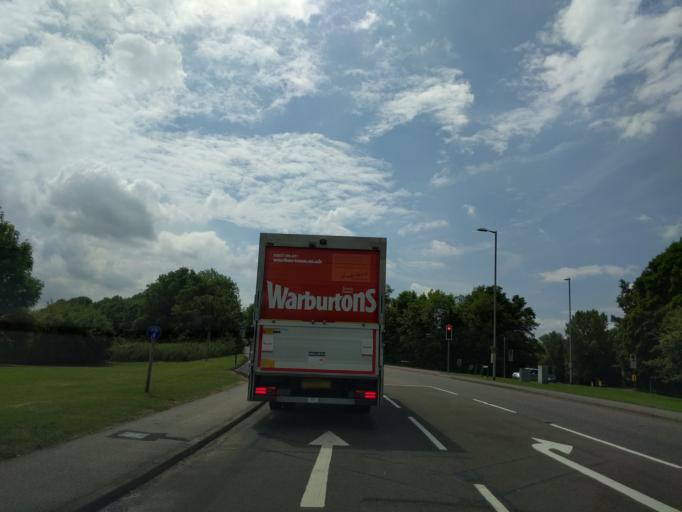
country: GB
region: England
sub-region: Cambridgeshire
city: Histon
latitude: 52.2376
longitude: 0.1118
